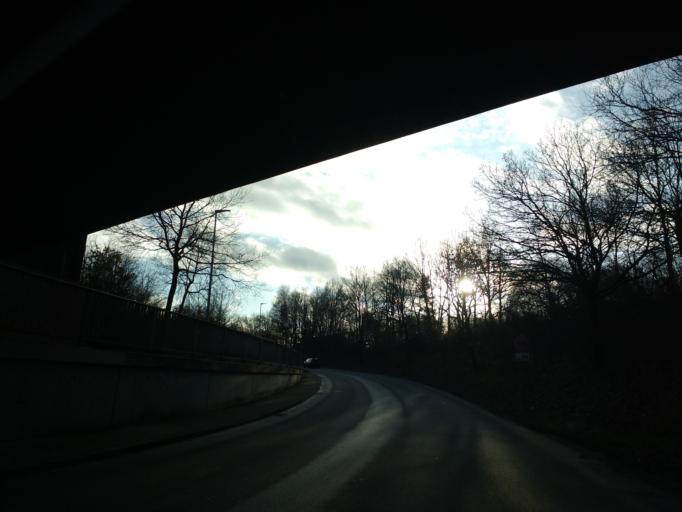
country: DE
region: Schleswig-Holstein
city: Kaltenkirchen
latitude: 53.8413
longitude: 9.9443
